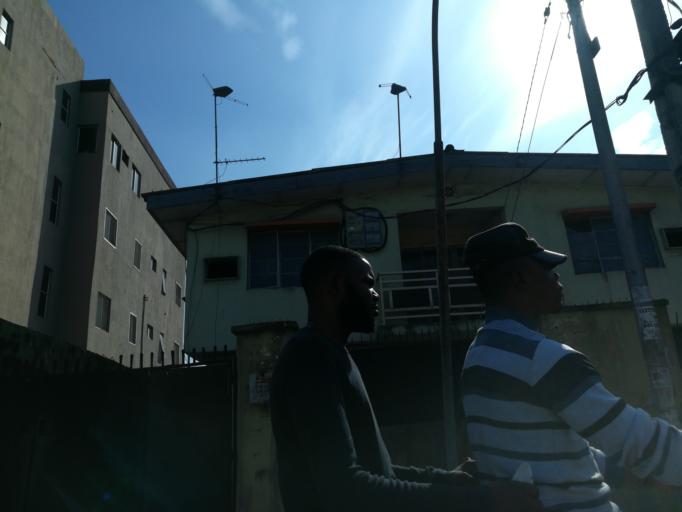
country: NG
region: Lagos
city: Ikeja
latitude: 6.6021
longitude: 3.3391
